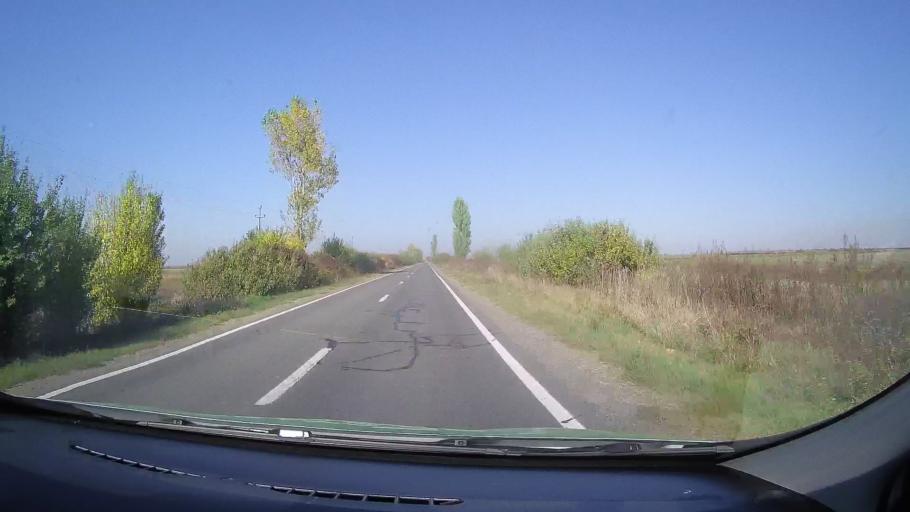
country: RO
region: Satu Mare
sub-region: Comuna Urziceni
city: Urziceni
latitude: 47.7073
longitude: 22.4311
